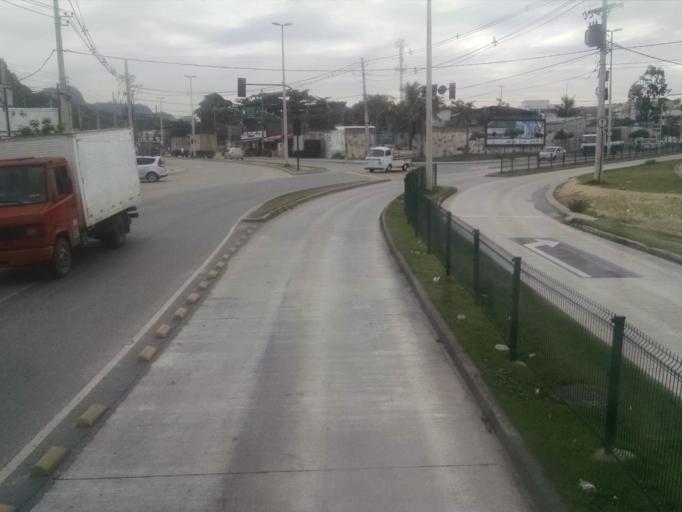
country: BR
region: Rio de Janeiro
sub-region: Nilopolis
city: Nilopolis
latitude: -22.9610
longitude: -43.3902
